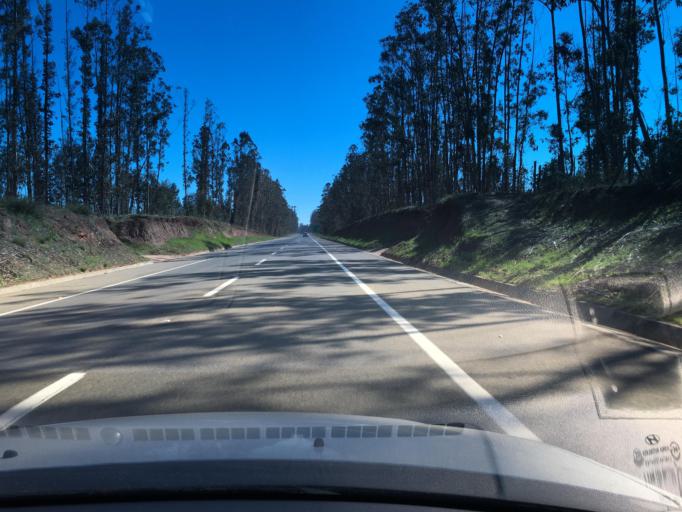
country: CL
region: Valparaiso
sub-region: San Antonio Province
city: El Tabo
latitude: -33.4028
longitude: -71.5758
